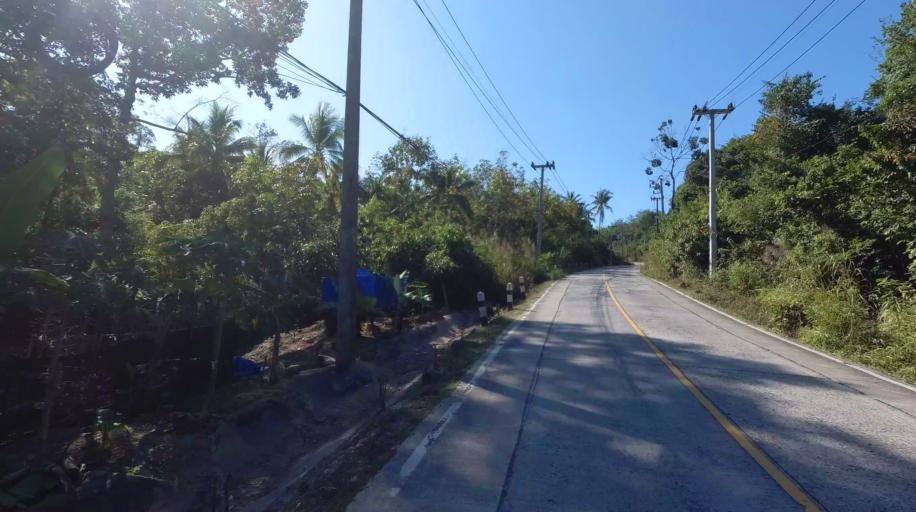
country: TH
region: Trat
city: Ko Kut
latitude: 11.6174
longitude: 102.5440
